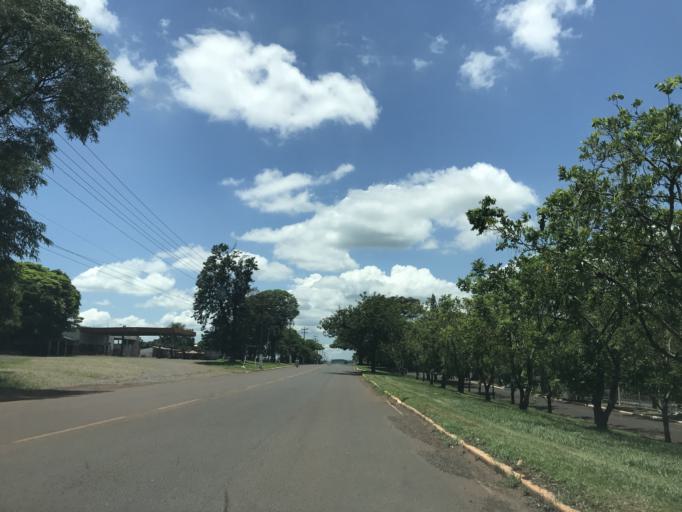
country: BR
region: Parana
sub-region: Marialva
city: Marialva
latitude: -23.4929
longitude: -51.7832
